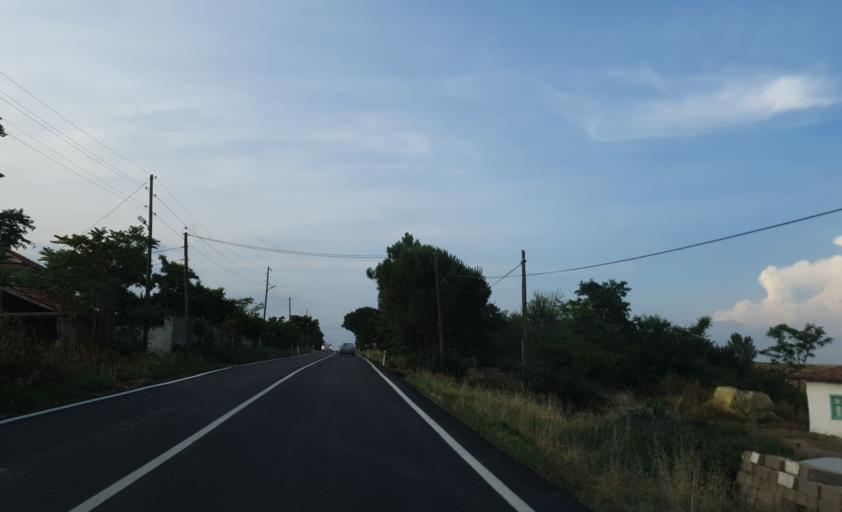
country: TR
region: Tekirdag
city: Hayrabolu
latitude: 41.2910
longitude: 27.1339
